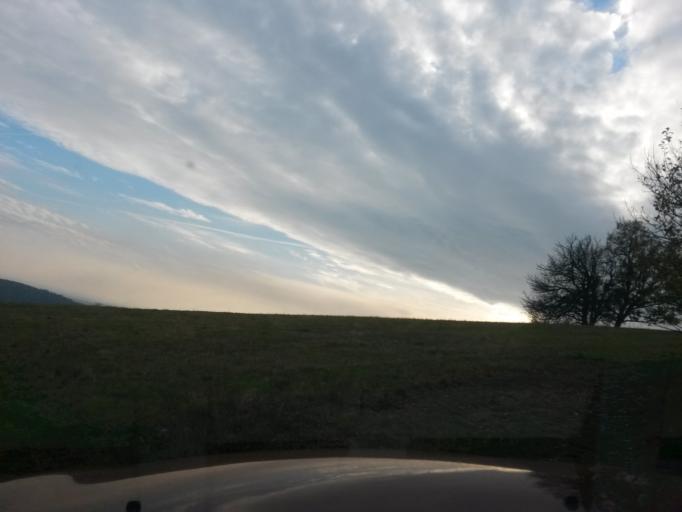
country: SK
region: Kosicky
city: Kosice
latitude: 48.7685
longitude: 21.2166
